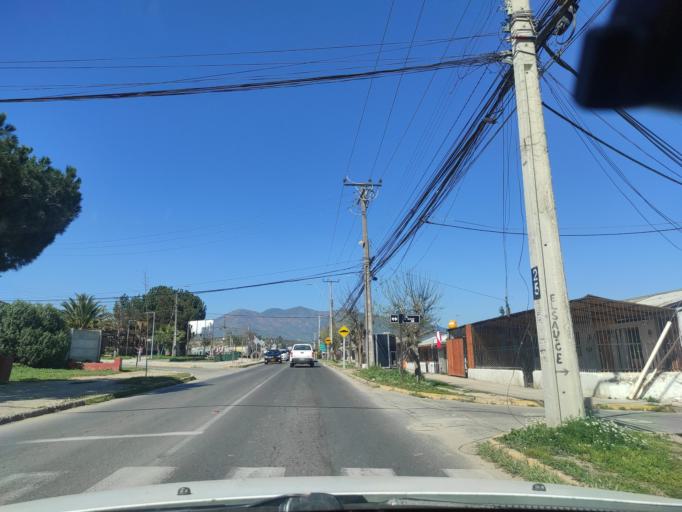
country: CL
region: Valparaiso
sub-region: Provincia de Marga Marga
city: Limache
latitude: -33.0131
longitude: -71.2535
